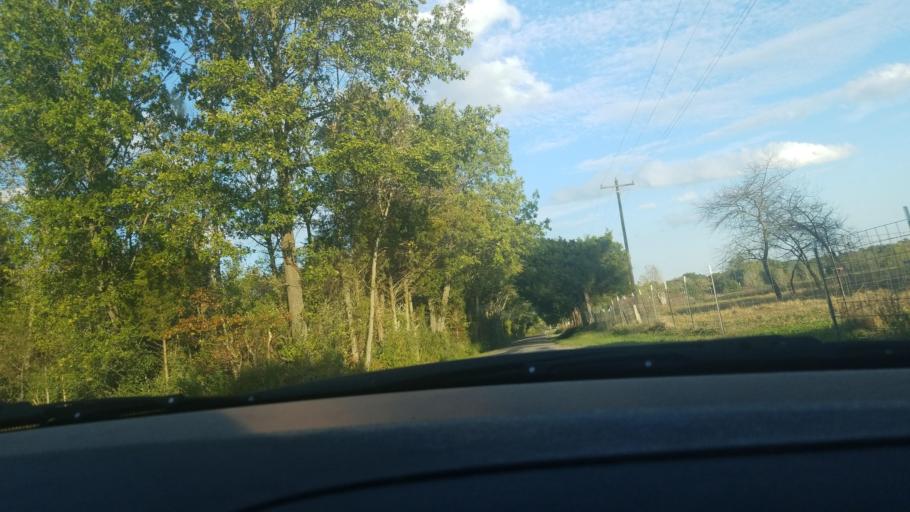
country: US
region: Illinois
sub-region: Saline County
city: Carrier Mills
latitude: 37.7721
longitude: -88.7213
